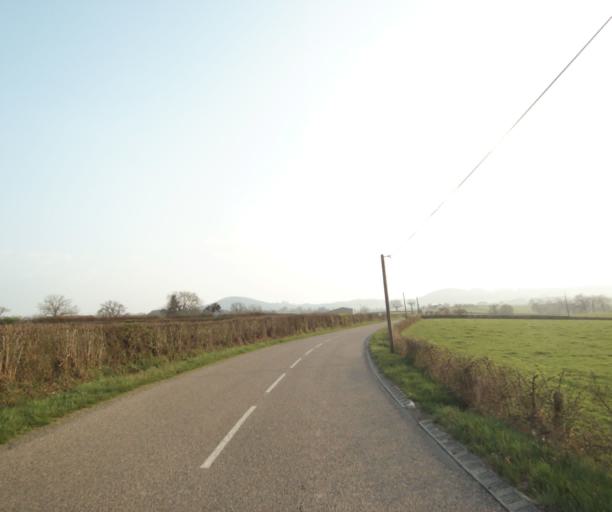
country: FR
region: Bourgogne
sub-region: Departement de Saone-et-Loire
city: Charolles
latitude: 46.4428
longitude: 4.4254
